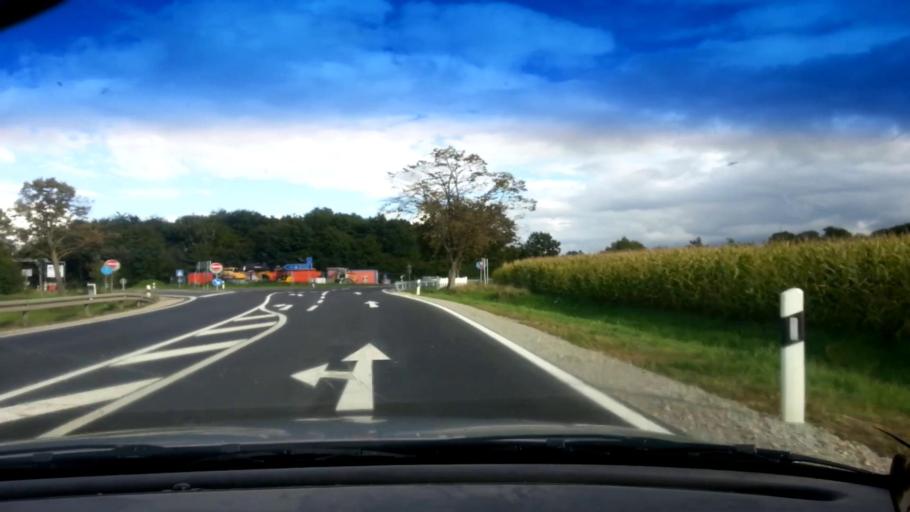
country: DE
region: Bavaria
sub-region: Upper Franconia
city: Ebensfeld
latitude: 50.0596
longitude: 10.9643
